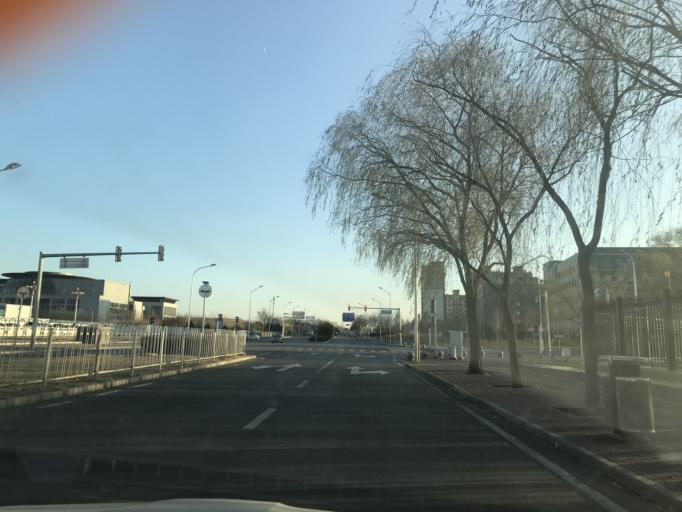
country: CN
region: Beijing
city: Xibeiwang
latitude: 40.0693
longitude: 116.2509
